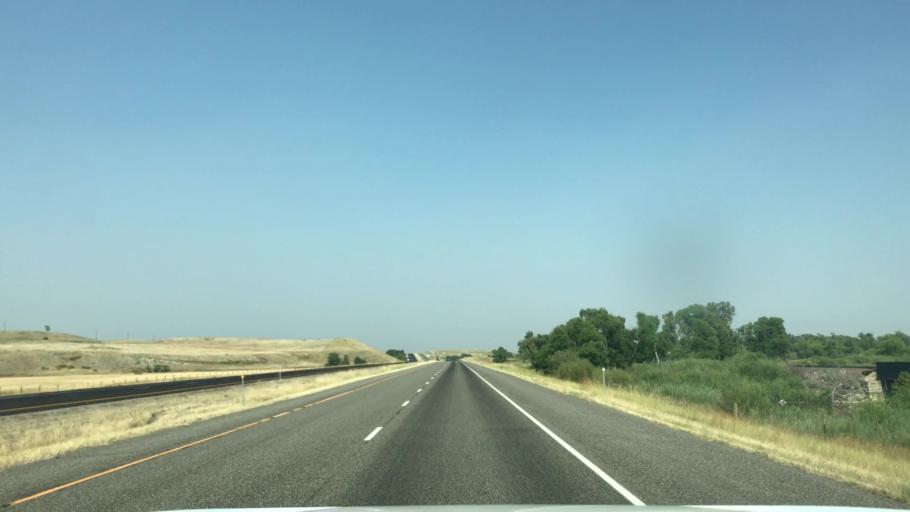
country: US
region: Montana
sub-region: Cascade County
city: Sun Prairie
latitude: 47.2372
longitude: -111.7391
